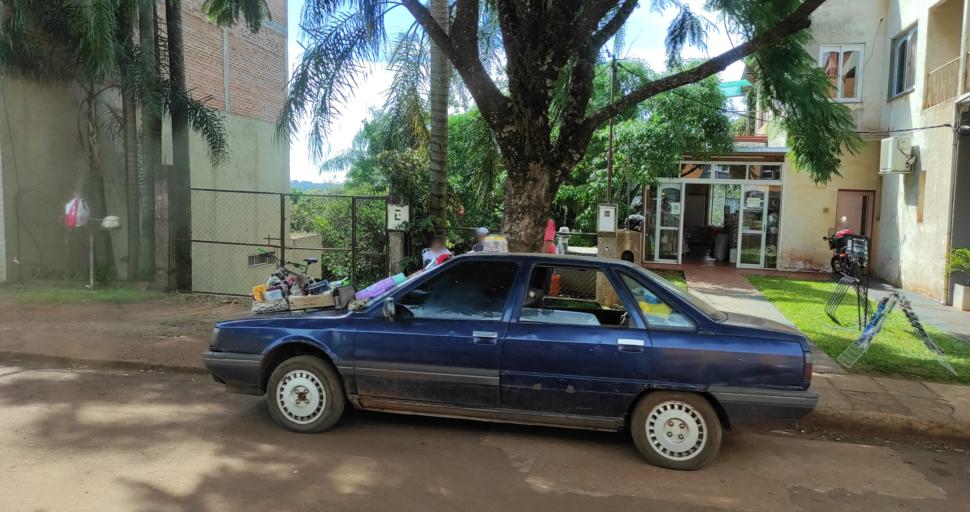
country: AR
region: Misiones
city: Dos de Mayo
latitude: -27.0253
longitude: -54.6865
